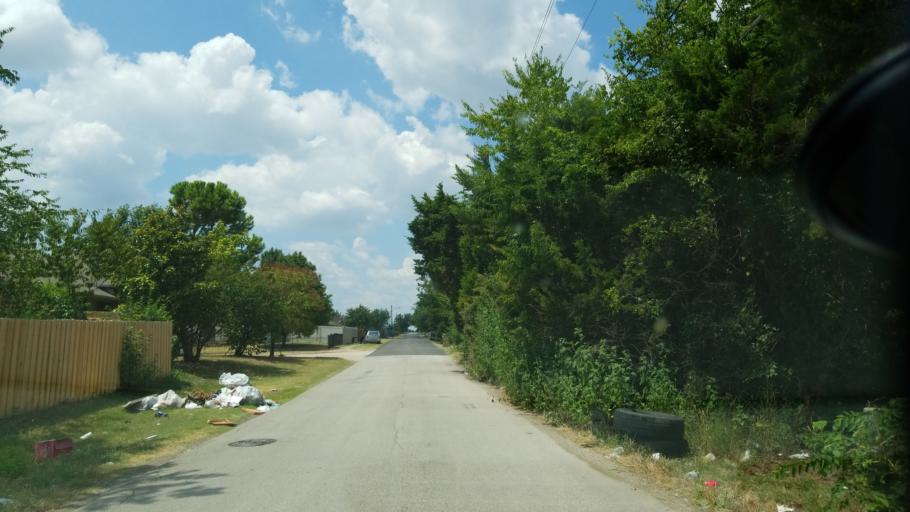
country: US
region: Texas
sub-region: Dallas County
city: Duncanville
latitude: 32.6814
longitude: -96.8948
